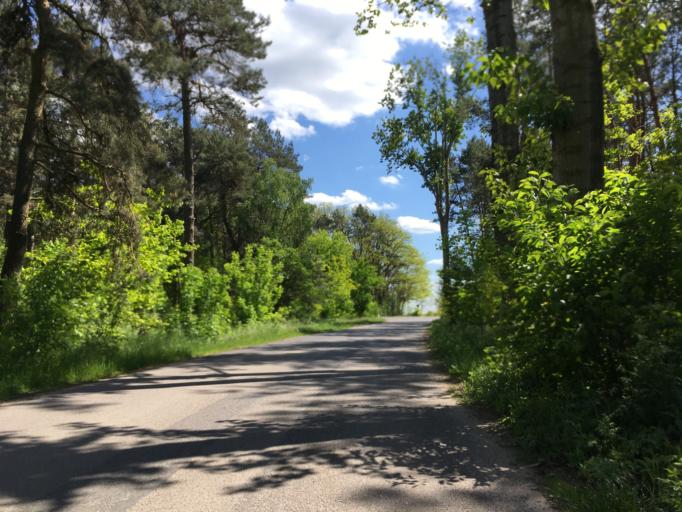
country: DE
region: Brandenburg
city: Rudnitz
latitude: 52.6971
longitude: 13.6680
